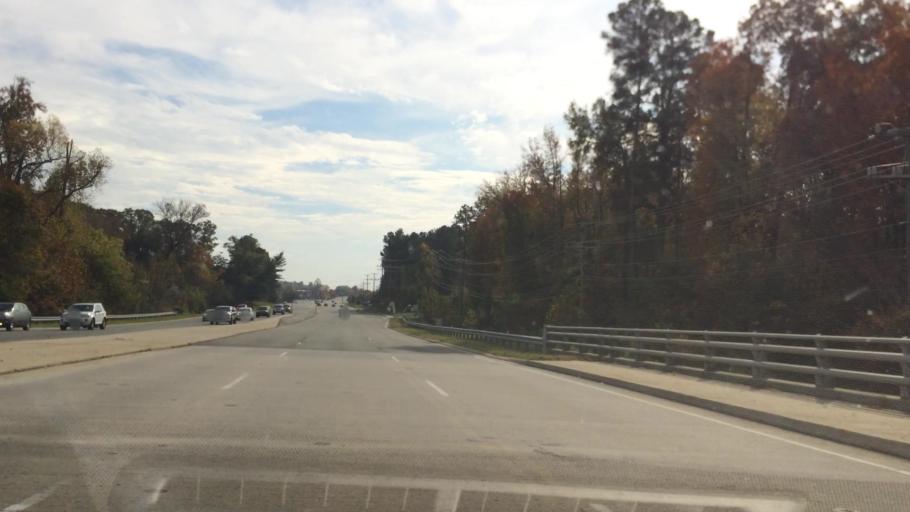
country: US
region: Virginia
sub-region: Henrico County
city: Glen Allen
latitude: 37.6803
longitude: -77.4618
